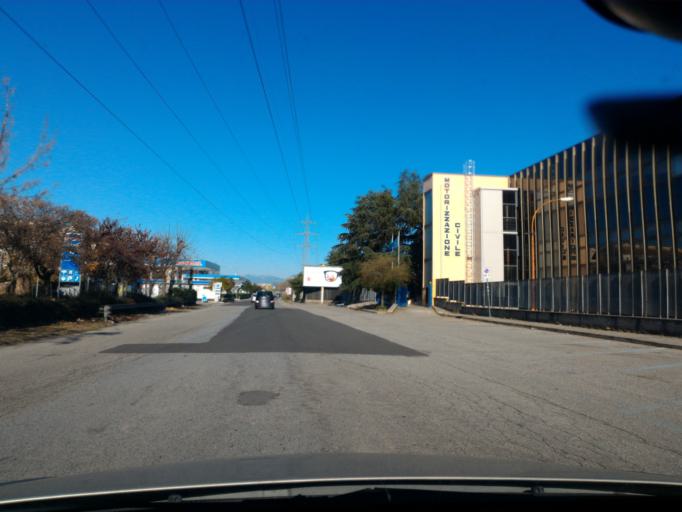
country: IT
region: Calabria
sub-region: Provincia di Cosenza
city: Cosenza
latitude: 39.3228
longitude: 16.2566
